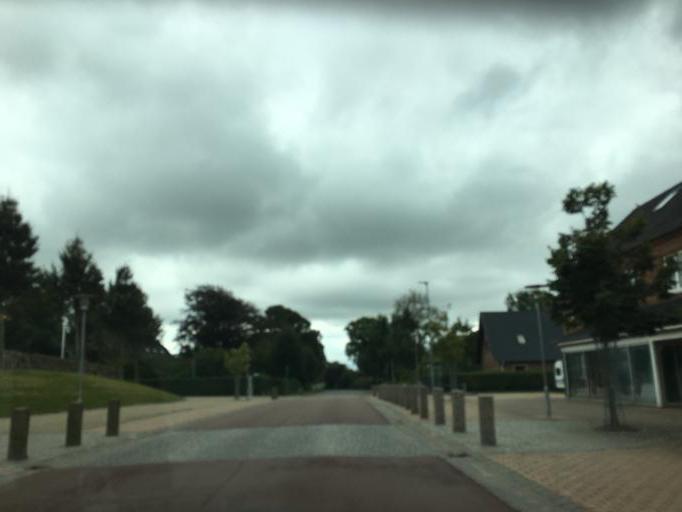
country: DK
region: South Denmark
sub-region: Kolding Kommune
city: Kolding
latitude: 55.5836
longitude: 9.4922
